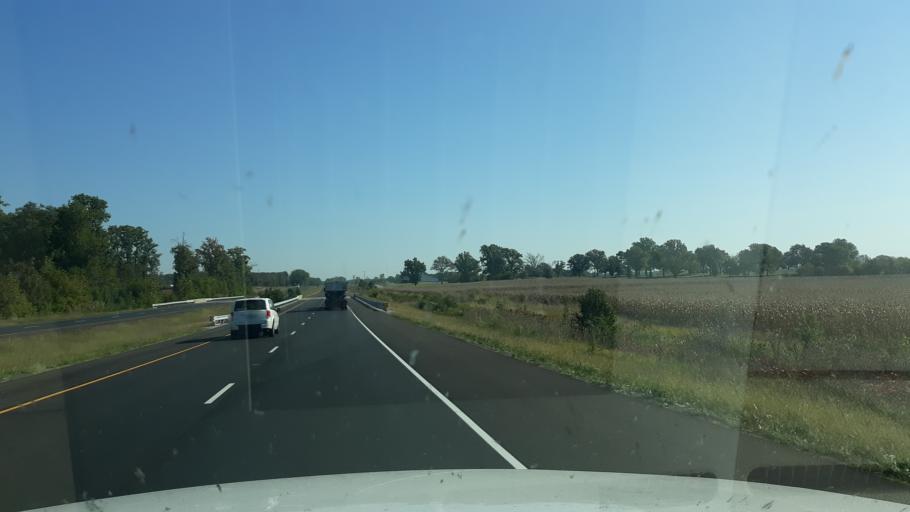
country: US
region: Illinois
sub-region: Saline County
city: Eldorado
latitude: 37.7952
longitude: -88.4711
